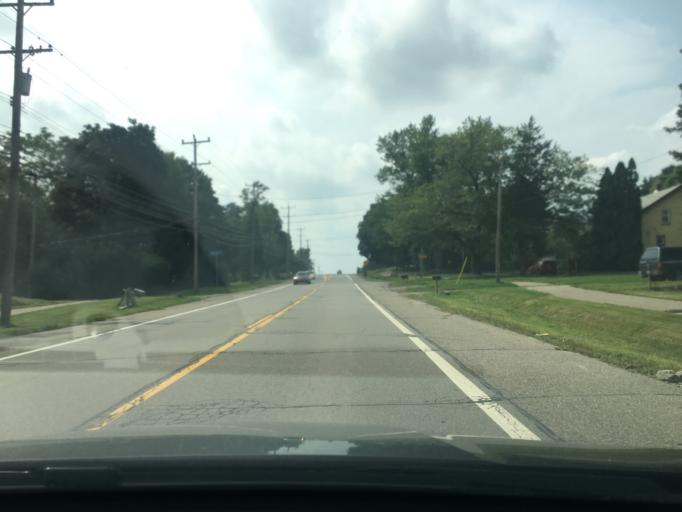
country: US
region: Michigan
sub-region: Oakland County
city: Rochester Hills
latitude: 42.6348
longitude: -83.1798
